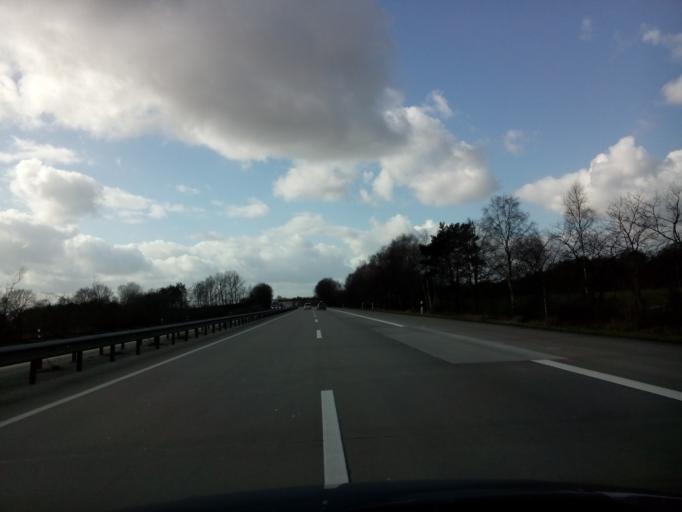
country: DE
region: Lower Saxony
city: Prinzhofte
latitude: 52.9470
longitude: 8.5305
